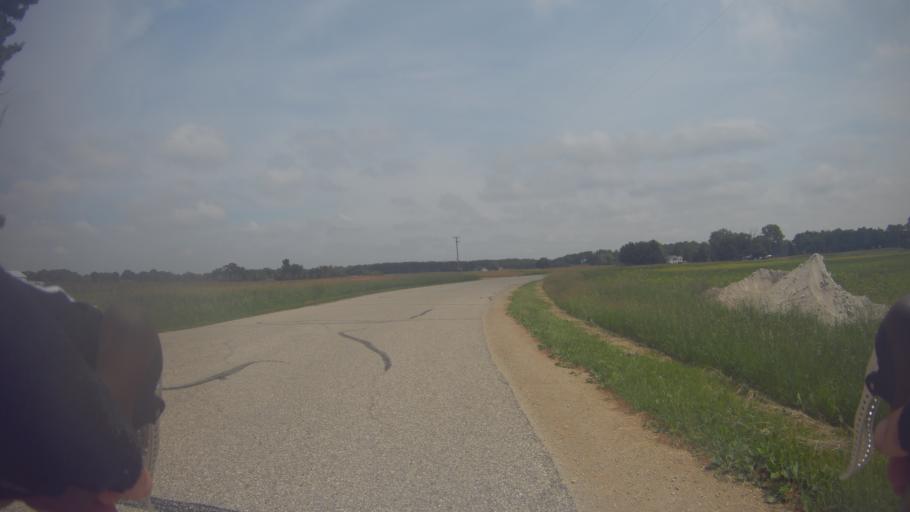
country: US
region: Wisconsin
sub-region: Jefferson County
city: Cambridge
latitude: 42.9675
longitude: -89.0088
